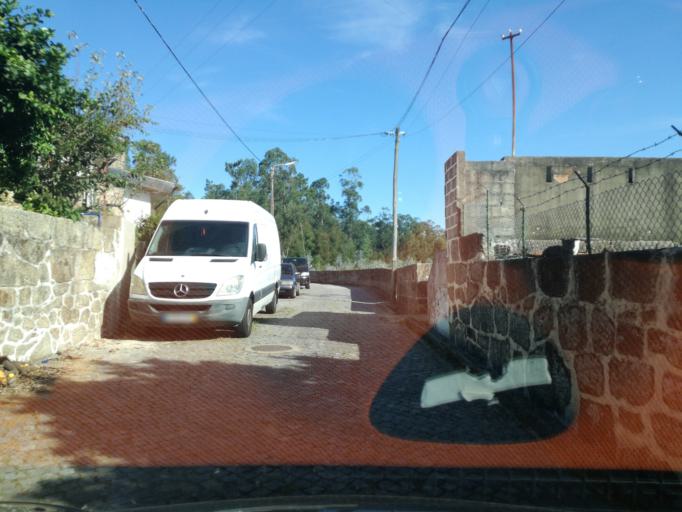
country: PT
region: Porto
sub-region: Maia
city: Anta
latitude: 41.2814
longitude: -8.6247
